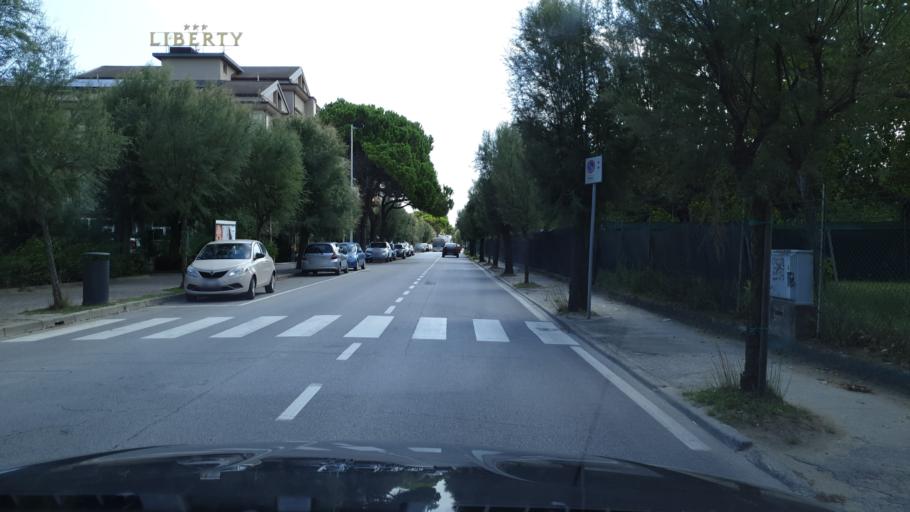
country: IT
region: Emilia-Romagna
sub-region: Provincia di Rimini
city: Misano Adriatico
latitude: 43.9903
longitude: 12.6803
